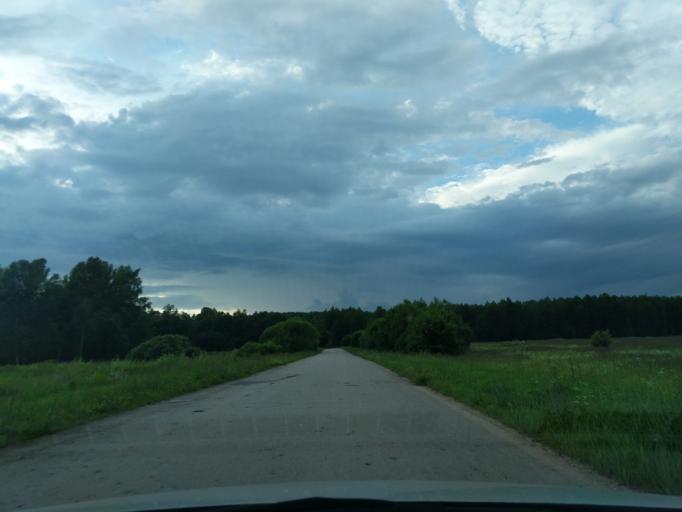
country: RU
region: Kaluga
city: Myatlevo
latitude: 54.8369
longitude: 35.6360
